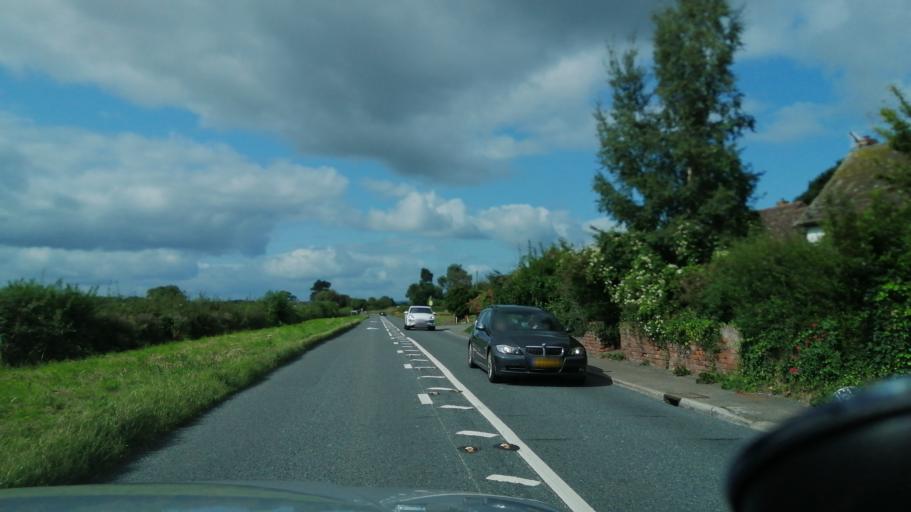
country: GB
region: England
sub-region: Herefordshire
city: Kinnersley
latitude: 52.1387
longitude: -2.9630
